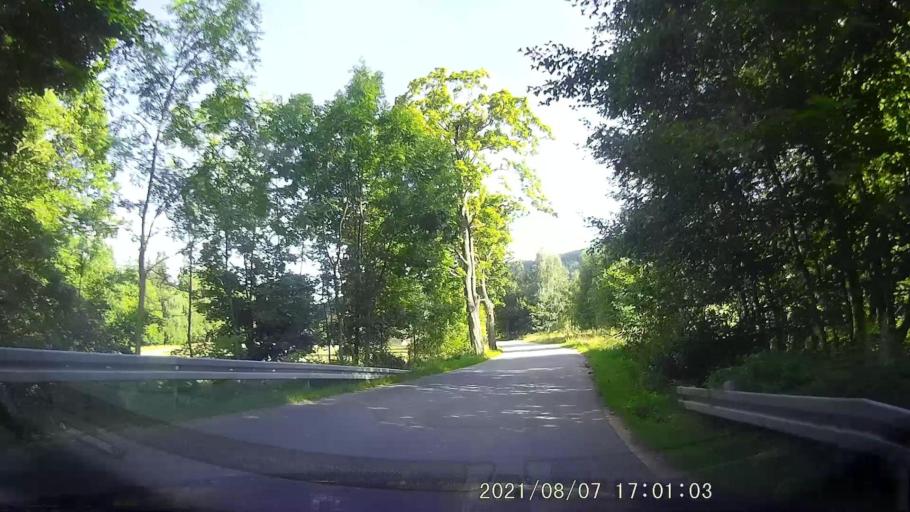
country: PL
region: Lower Silesian Voivodeship
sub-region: Powiat klodzki
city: Bystrzyca Klodzka
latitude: 50.2901
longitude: 16.5511
